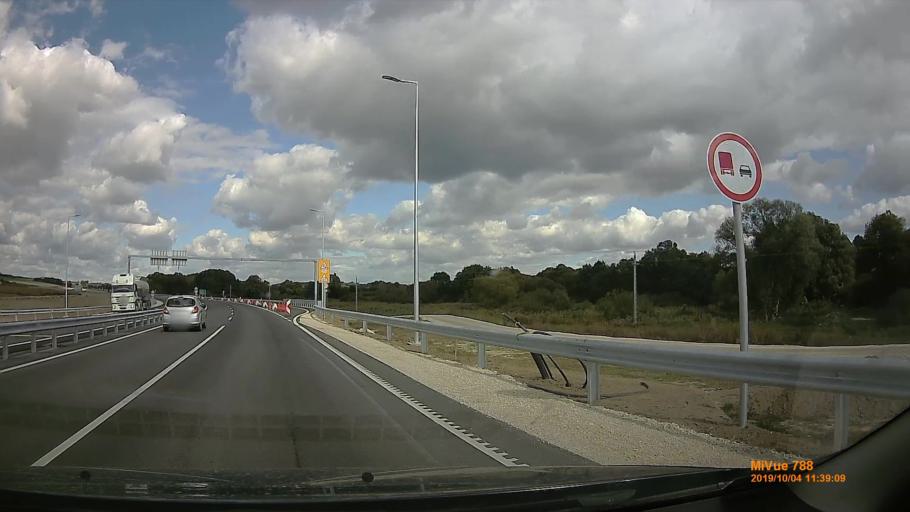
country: HU
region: Somogy
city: Karad
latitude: 46.5527
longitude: 17.8148
